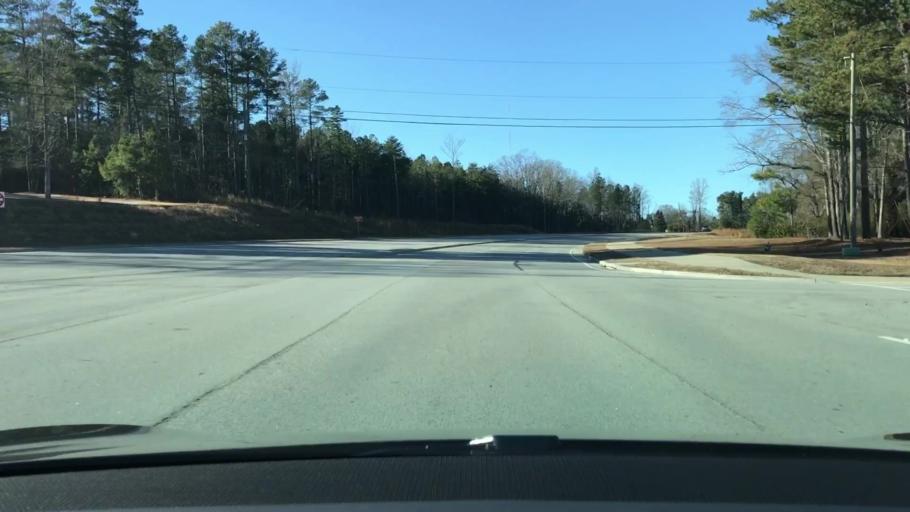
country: US
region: Georgia
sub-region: Hall County
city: Flowery Branch
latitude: 34.1226
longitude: -83.9181
